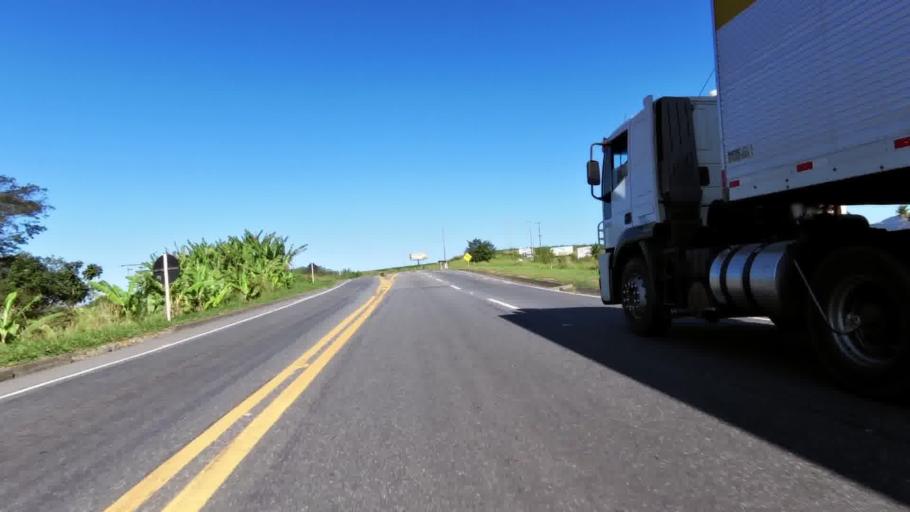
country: BR
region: Espirito Santo
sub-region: Alfredo Chaves
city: Alfredo Chaves
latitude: -20.6900
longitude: -40.7000
